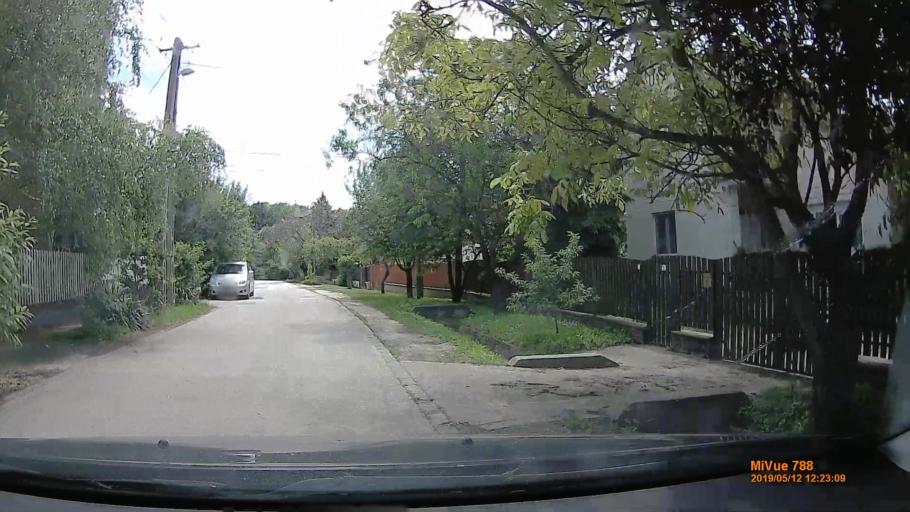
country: HU
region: Pest
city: Ecser
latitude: 47.4587
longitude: 19.2948
